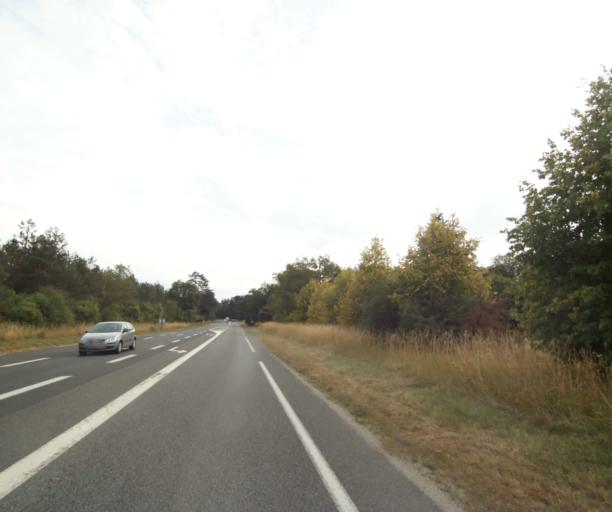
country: FR
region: Ile-de-France
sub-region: Departement de Seine-et-Marne
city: Bois-le-Roi
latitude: 48.4412
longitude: 2.6899
